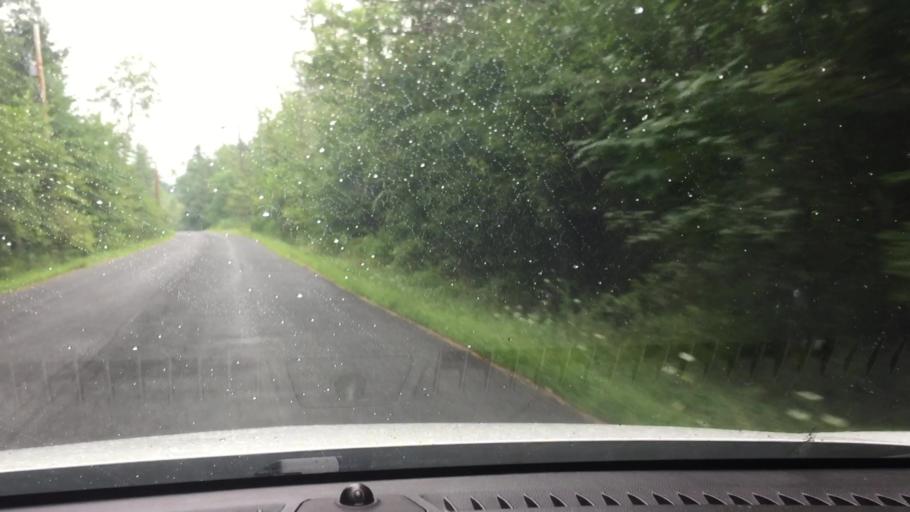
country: US
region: Massachusetts
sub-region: Berkshire County
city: Lee
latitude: 42.3089
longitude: -73.2841
